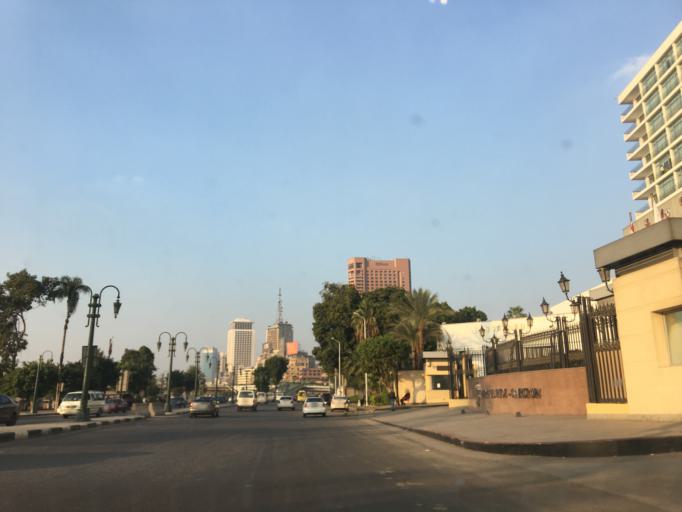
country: EG
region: Muhafazat al Qahirah
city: Cairo
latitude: 30.0457
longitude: 31.2317
